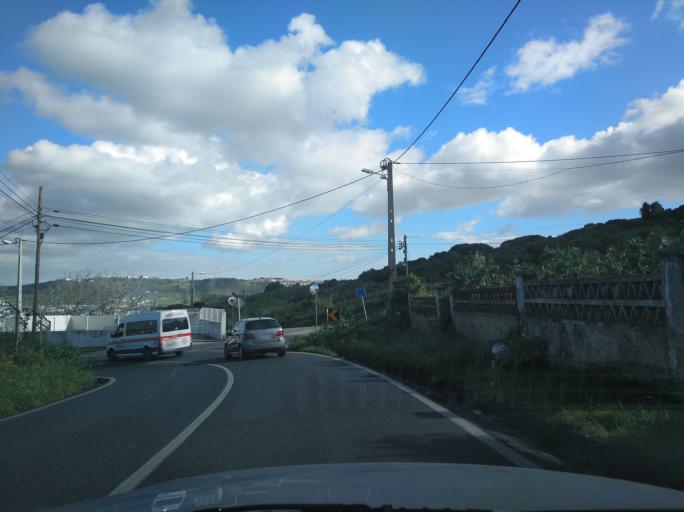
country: PT
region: Lisbon
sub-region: Loures
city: Loures
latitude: 38.8240
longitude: -9.1693
